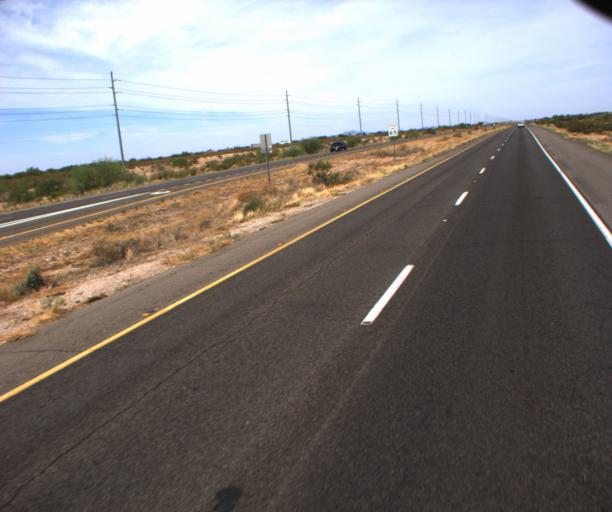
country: US
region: Arizona
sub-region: Maricopa County
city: Sun City West
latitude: 33.7413
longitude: -112.4815
